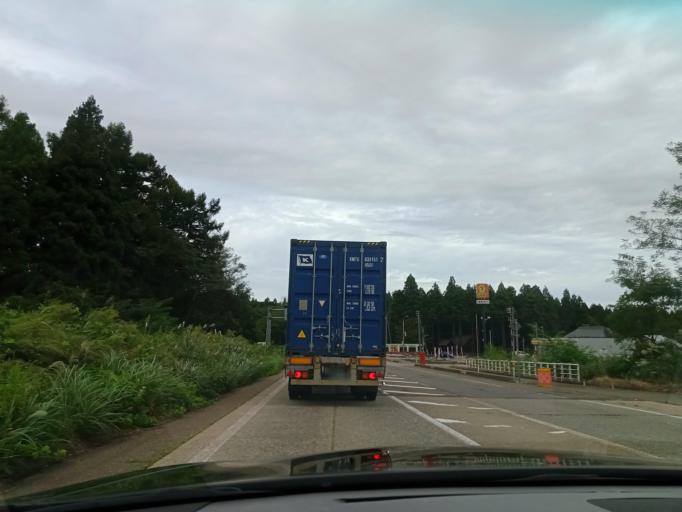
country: JP
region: Niigata
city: Arai
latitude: 36.9815
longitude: 138.2212
